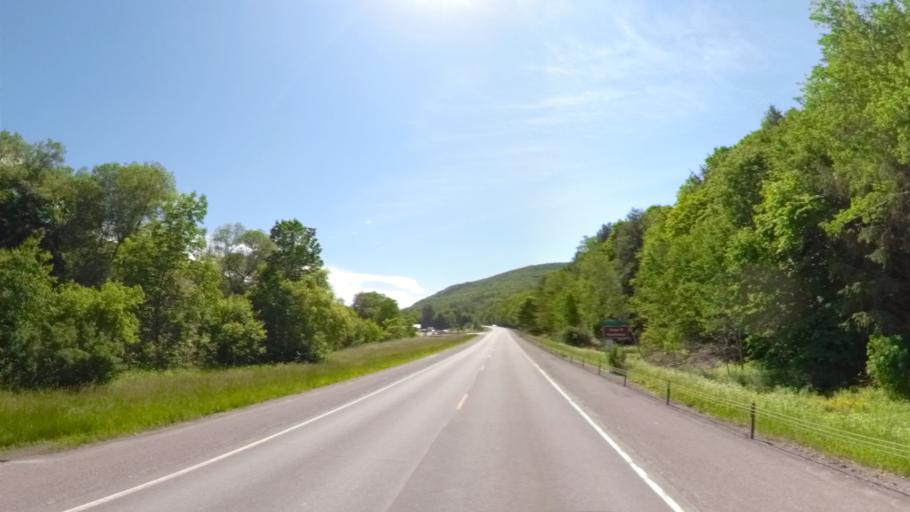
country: US
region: New York
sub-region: Delaware County
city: Stamford
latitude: 42.1560
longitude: -74.5484
